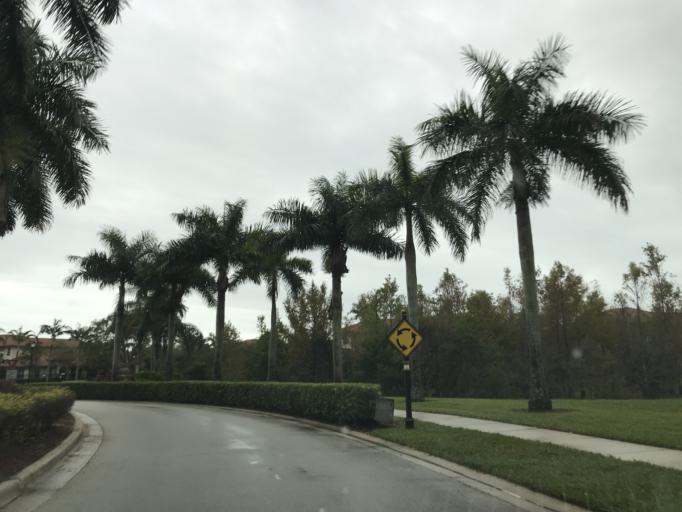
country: US
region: Florida
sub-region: Broward County
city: Coral Springs
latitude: 26.3066
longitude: -80.2844
